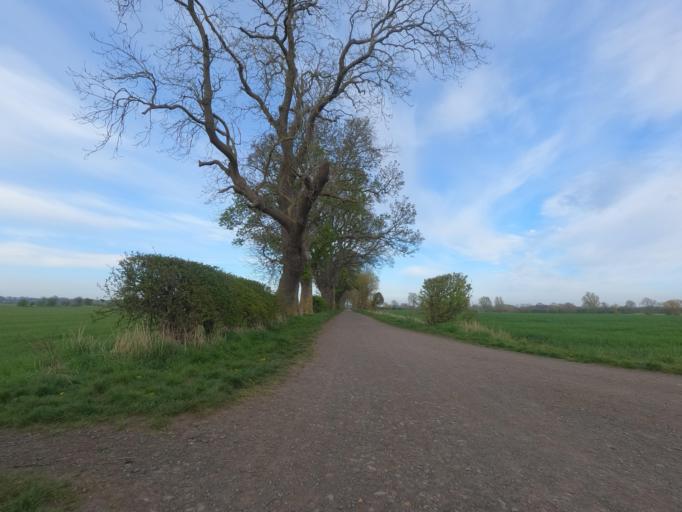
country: GB
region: England
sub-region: Newcastle upon Tyne
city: Dinnington
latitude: 55.0564
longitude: -1.6641
